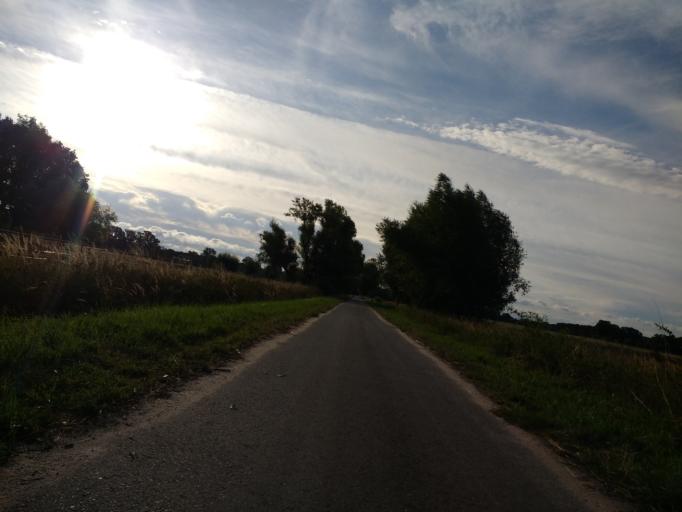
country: DE
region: Lower Saxony
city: Gifhorn
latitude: 52.4522
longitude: 10.5446
